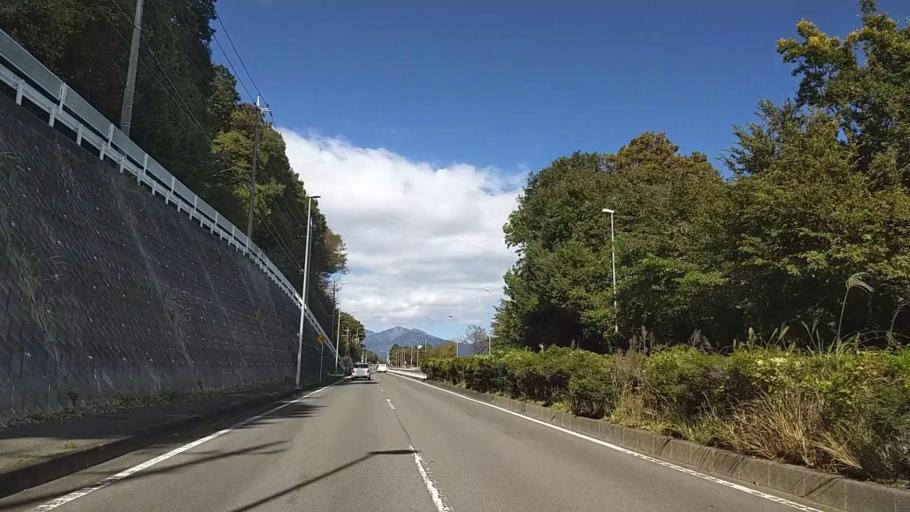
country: JP
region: Kanagawa
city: Ninomiya
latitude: 35.3296
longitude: 139.2324
